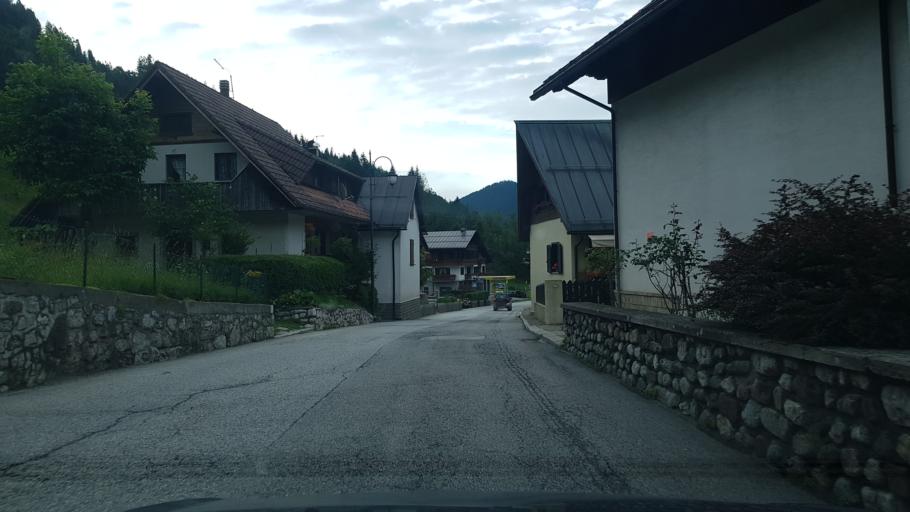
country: IT
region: Friuli Venezia Giulia
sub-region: Provincia di Udine
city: Forni Avoltri
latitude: 46.5847
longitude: 12.7803
